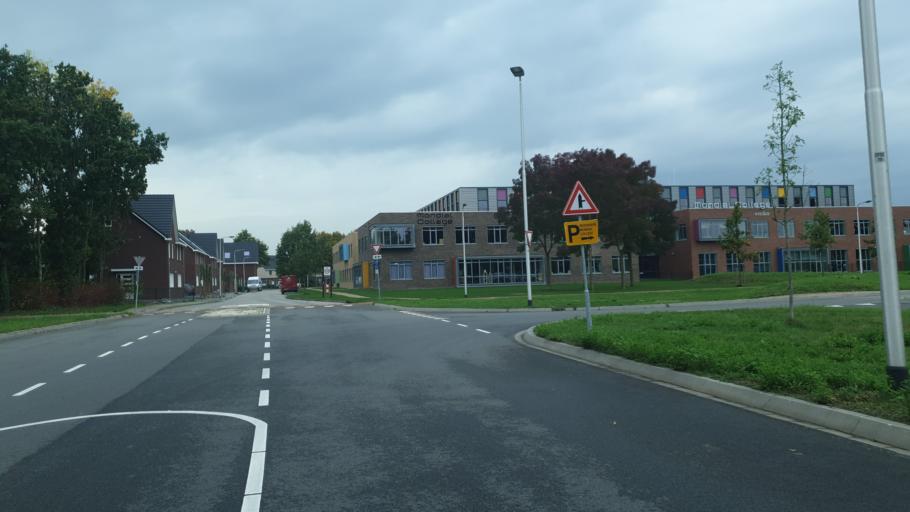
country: NL
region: Gelderland
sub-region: Gemeente Nijmegen
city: Lindenholt
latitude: 51.8364
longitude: 5.8014
